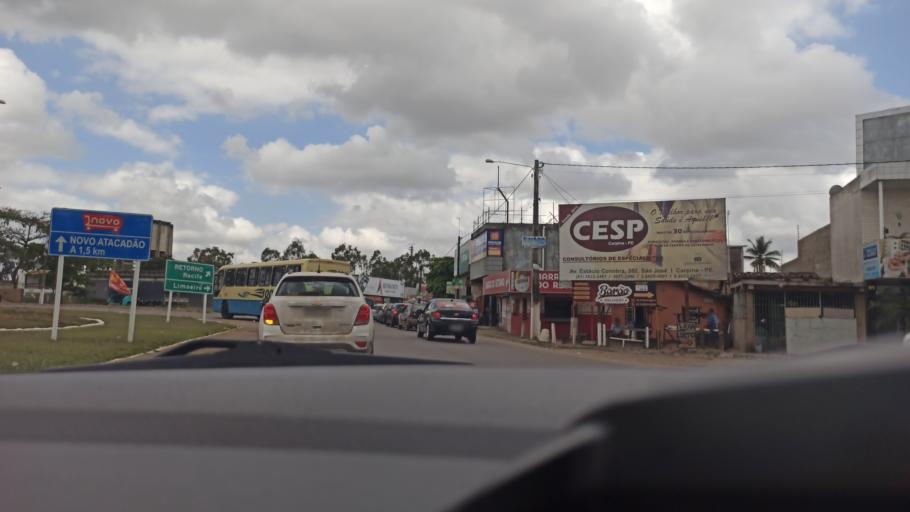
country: BR
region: Pernambuco
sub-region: Carpina
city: Carpina
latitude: -7.8464
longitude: -35.2398
